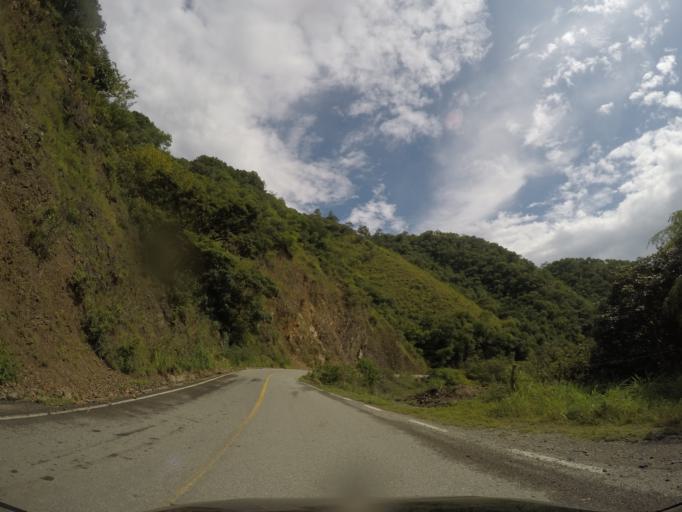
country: MX
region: Oaxaca
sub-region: San Jeronimo Coatlan
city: San Cristobal Honduras
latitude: 16.3721
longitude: -97.0830
